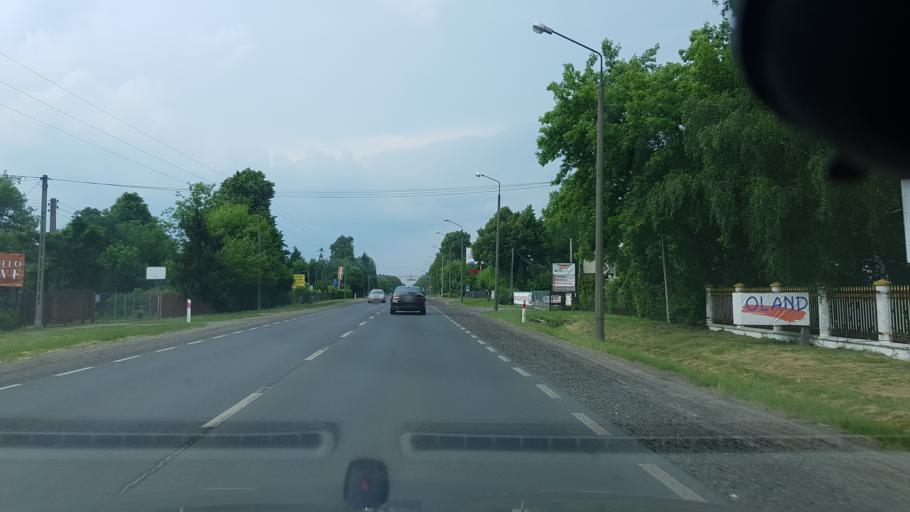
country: PL
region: Masovian Voivodeship
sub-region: Powiat legionowski
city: Michalow-Reginow
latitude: 52.4253
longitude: 20.9765
